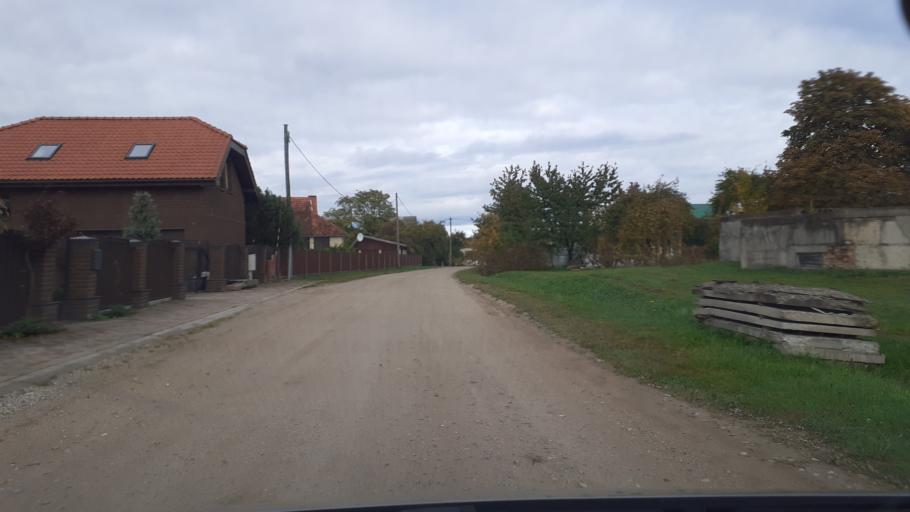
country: LV
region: Kuldigas Rajons
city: Kuldiga
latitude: 56.9655
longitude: 21.9928
